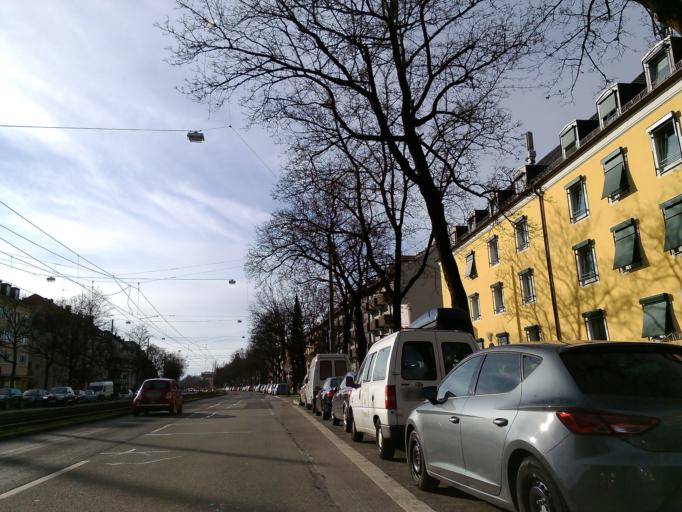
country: DE
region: Bavaria
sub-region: Upper Bavaria
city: Munich
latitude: 48.1078
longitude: 11.5731
